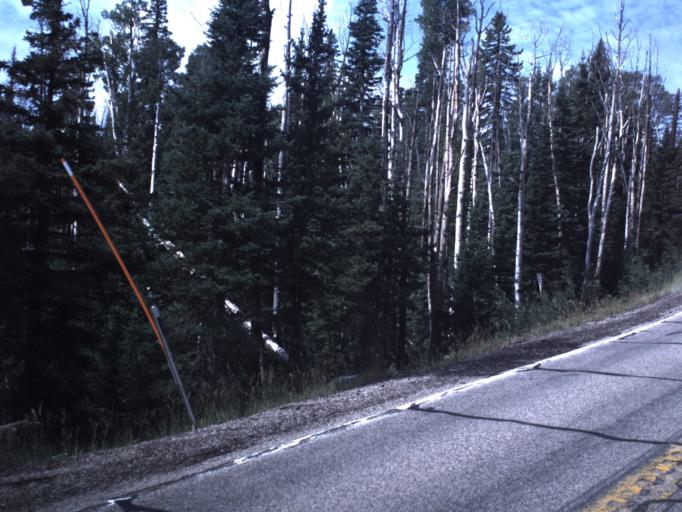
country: US
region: Utah
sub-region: Iron County
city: Parowan
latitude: 37.5198
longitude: -112.7073
